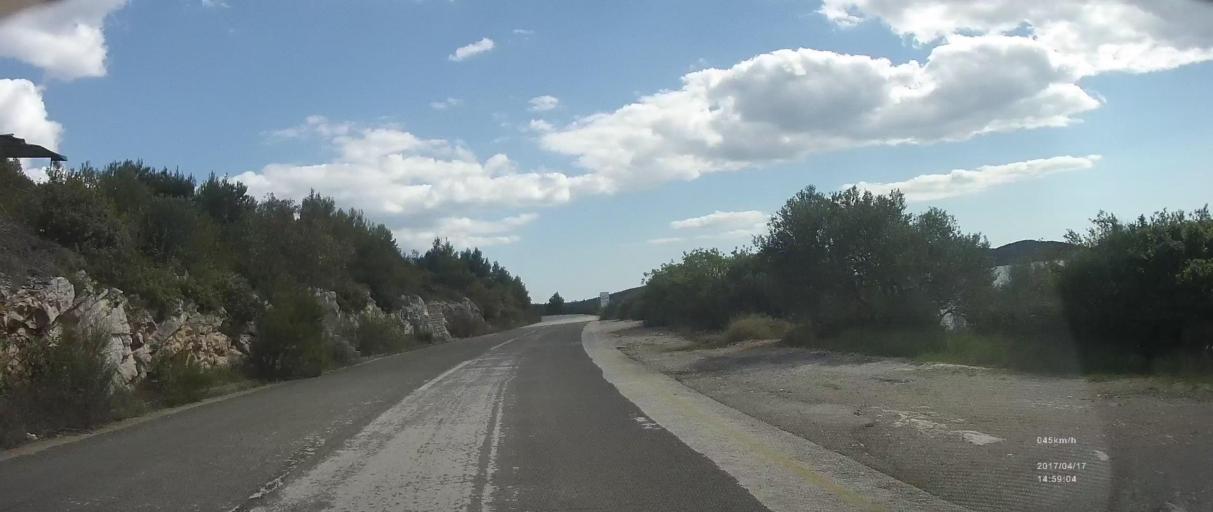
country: HR
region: Sibensko-Kniniska
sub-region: Grad Sibenik
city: Tisno
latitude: 43.8361
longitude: 15.6317
